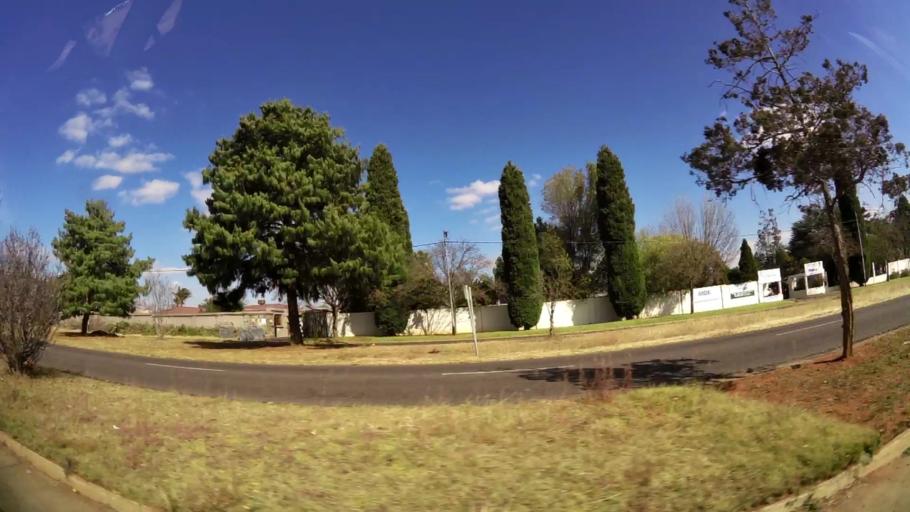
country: ZA
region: Gauteng
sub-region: West Rand District Municipality
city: Krugersdorp
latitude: -26.0953
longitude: 27.7915
